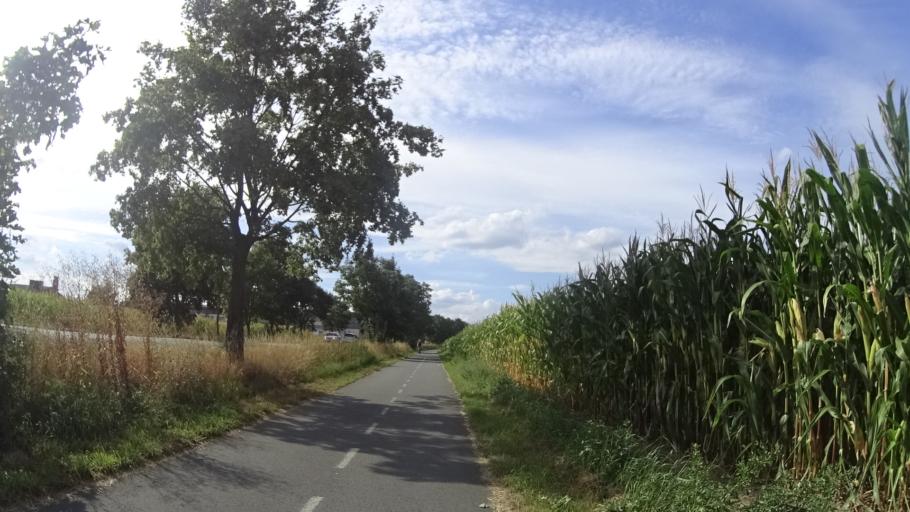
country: CZ
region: Olomoucky
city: Moravicany
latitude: 49.7700
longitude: 16.9447
